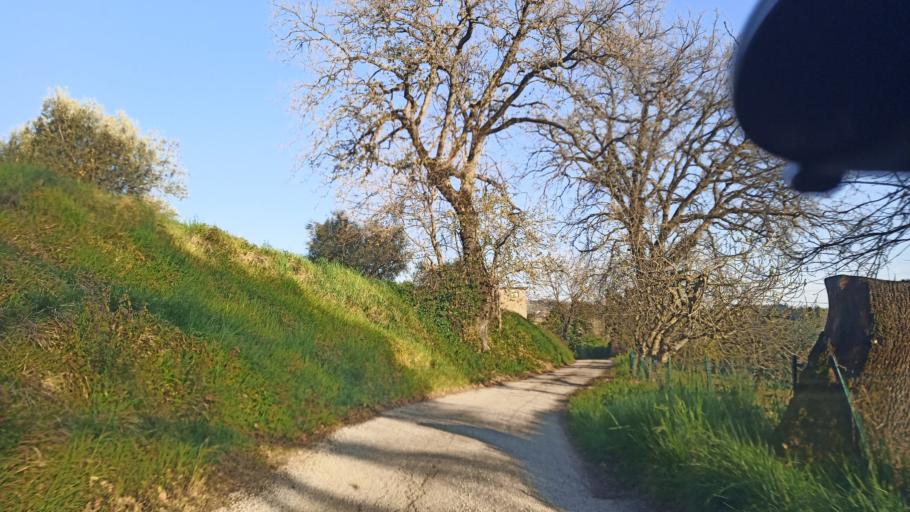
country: IT
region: Latium
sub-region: Provincia di Rieti
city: Poggio Mirteto
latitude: 42.2638
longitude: 12.6630
